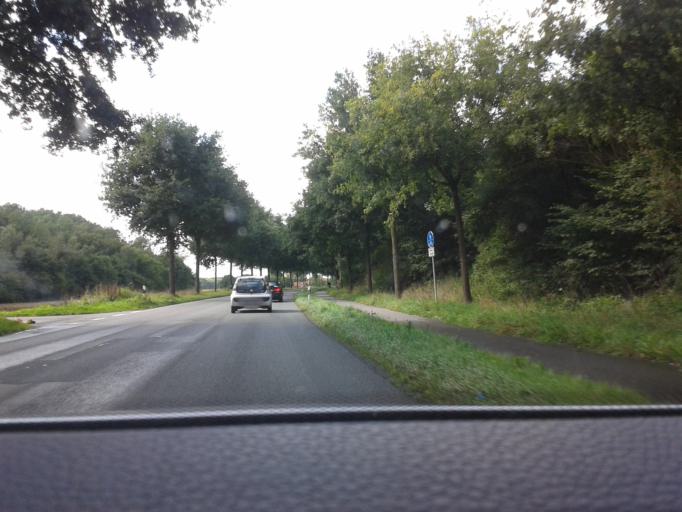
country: DE
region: North Rhine-Westphalia
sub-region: Regierungsbezirk Dusseldorf
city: Weeze
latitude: 51.6173
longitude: 6.1950
